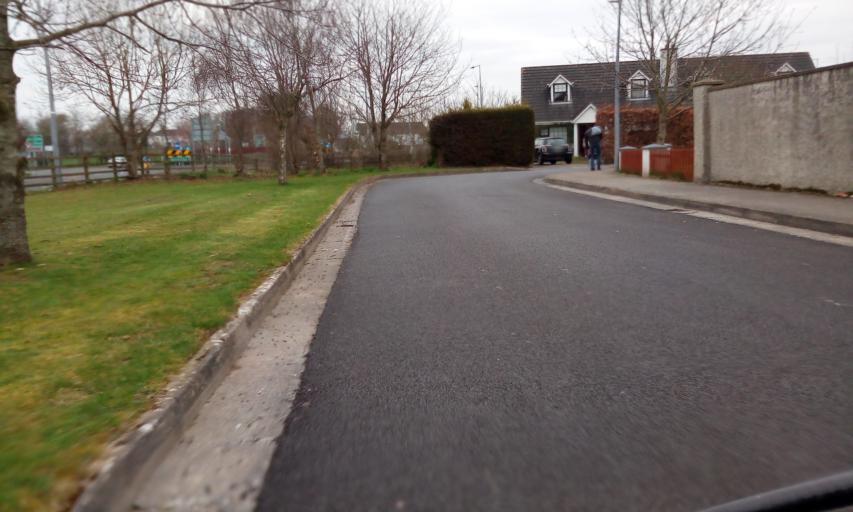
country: IE
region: Leinster
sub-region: Kilkenny
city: Kilkenny
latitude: 52.6635
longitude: -7.2289
